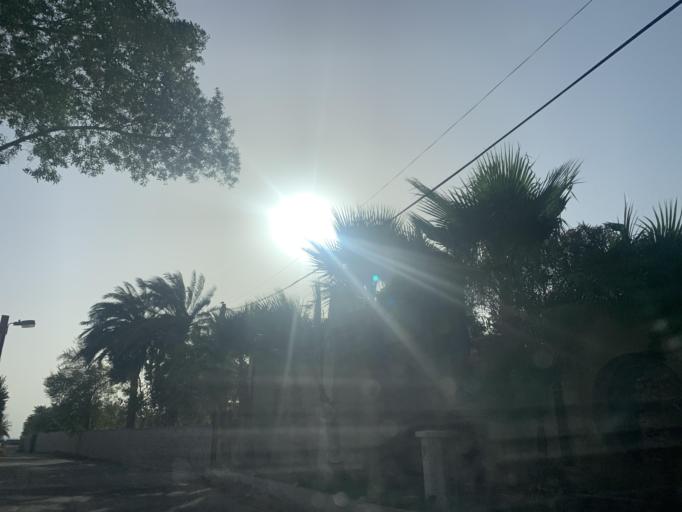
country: BH
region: Central Governorate
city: Madinat Hamad
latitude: 26.1879
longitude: 50.4607
